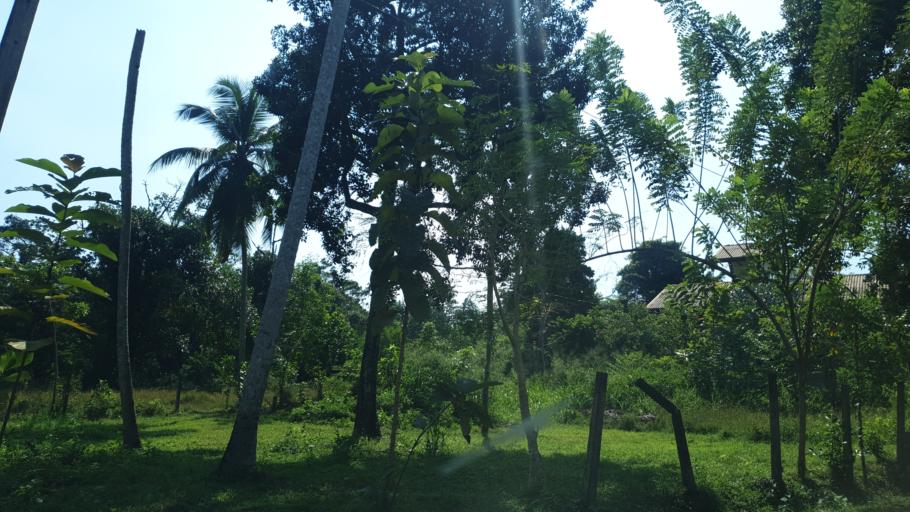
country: LK
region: Western
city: Moratuwa
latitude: 6.7667
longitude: 79.9201
